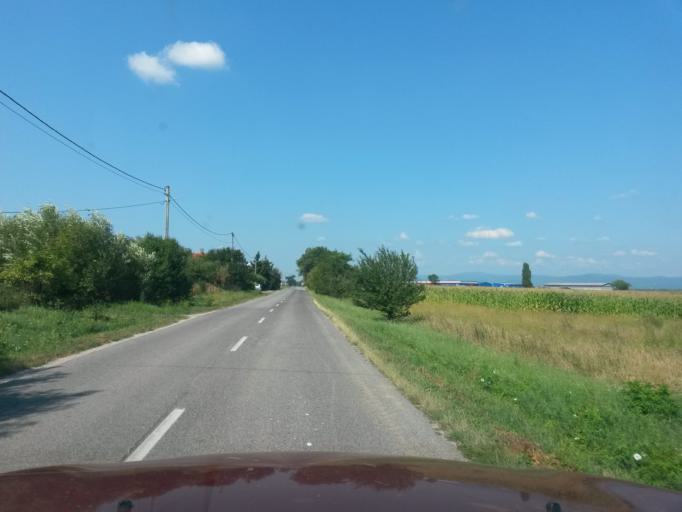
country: SK
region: Kosicky
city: Moldava nad Bodvou
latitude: 48.5329
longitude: 21.0948
